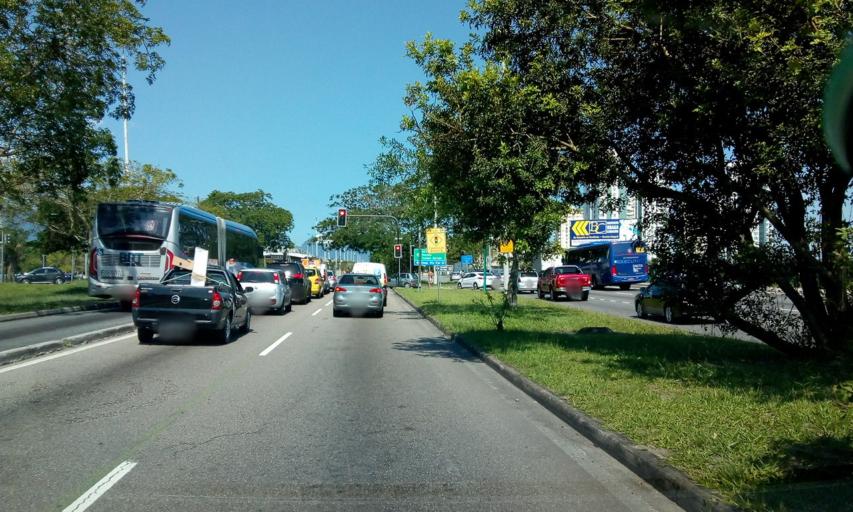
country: BR
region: Rio de Janeiro
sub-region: Nilopolis
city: Nilopolis
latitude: -23.0000
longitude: -43.4087
